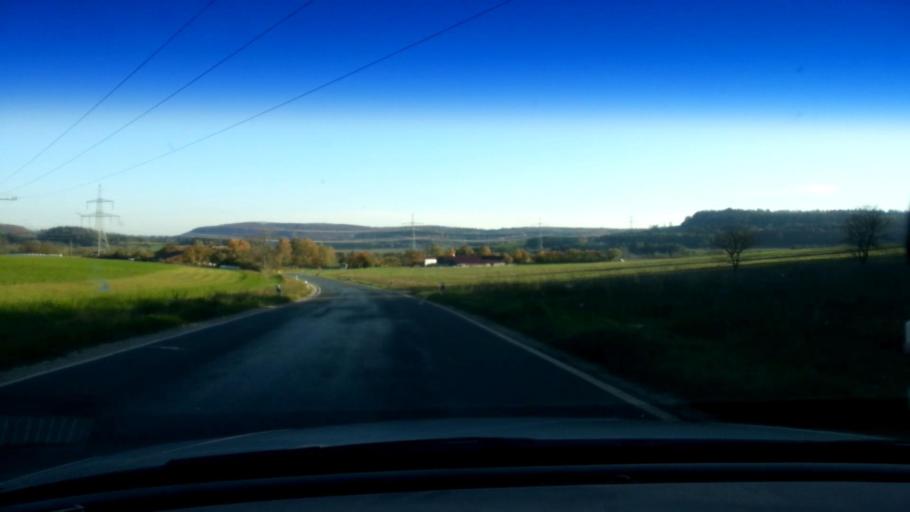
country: DE
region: Bavaria
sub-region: Upper Franconia
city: Poxdorf
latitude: 49.8954
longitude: 11.1002
